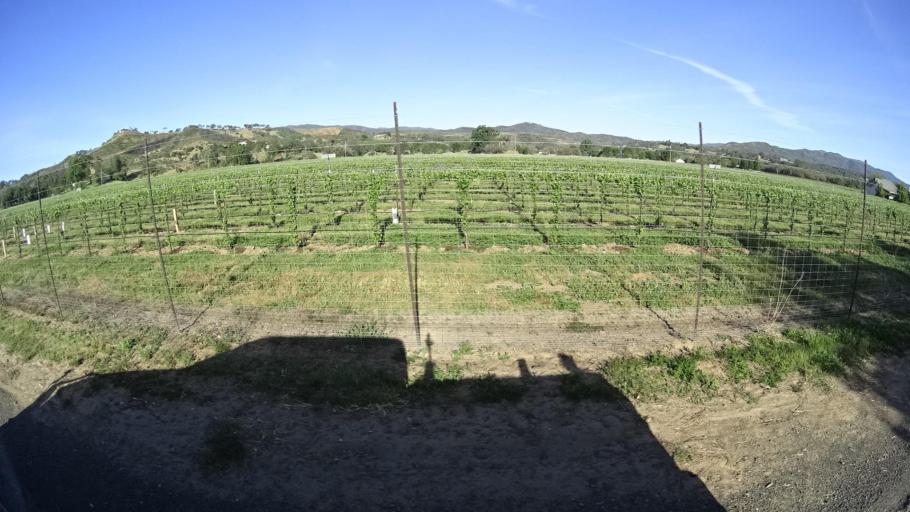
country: US
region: California
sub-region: Lake County
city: Lakeport
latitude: 39.0682
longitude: -122.9498
